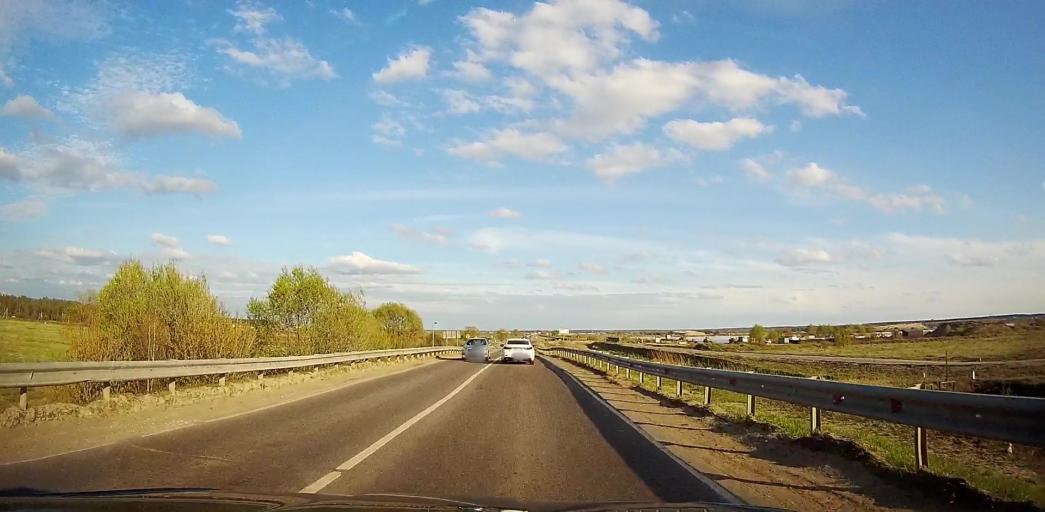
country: RU
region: Moskovskaya
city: Ramenskoye
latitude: 55.5141
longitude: 38.2760
